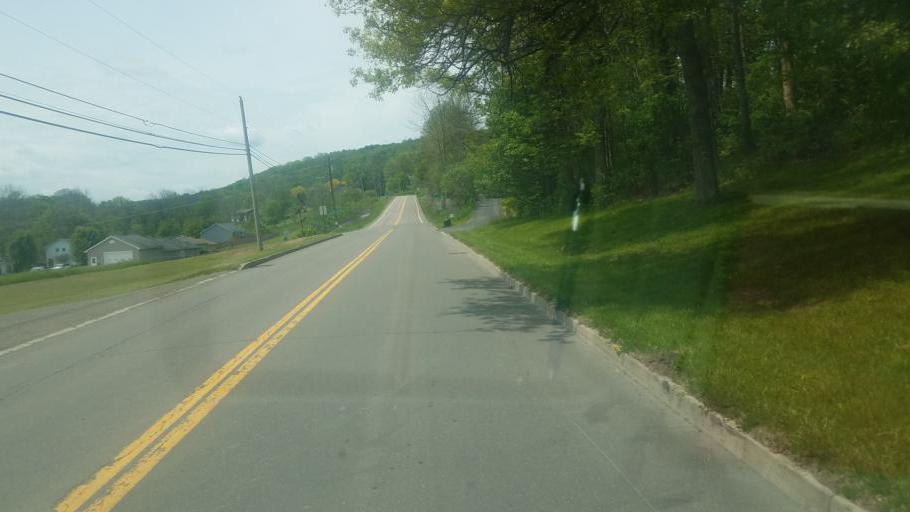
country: US
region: Pennsylvania
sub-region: Tioga County
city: Wellsboro
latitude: 41.7430
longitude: -77.3197
